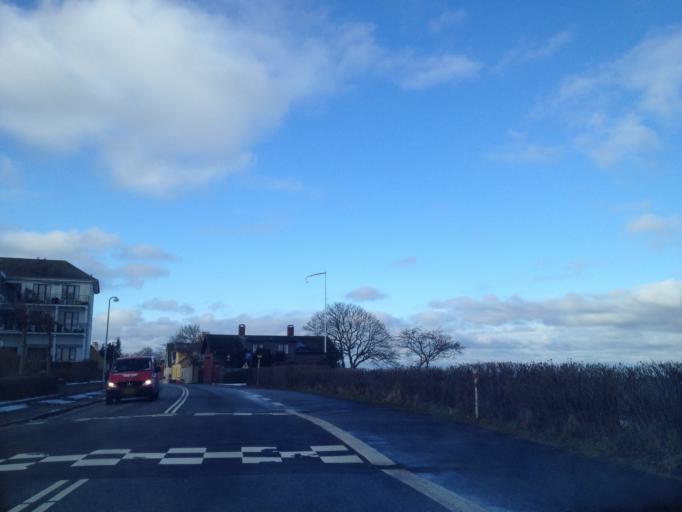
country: DK
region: Capital Region
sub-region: Helsingor Kommune
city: Hellebaek
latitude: 56.0700
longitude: 12.5581
